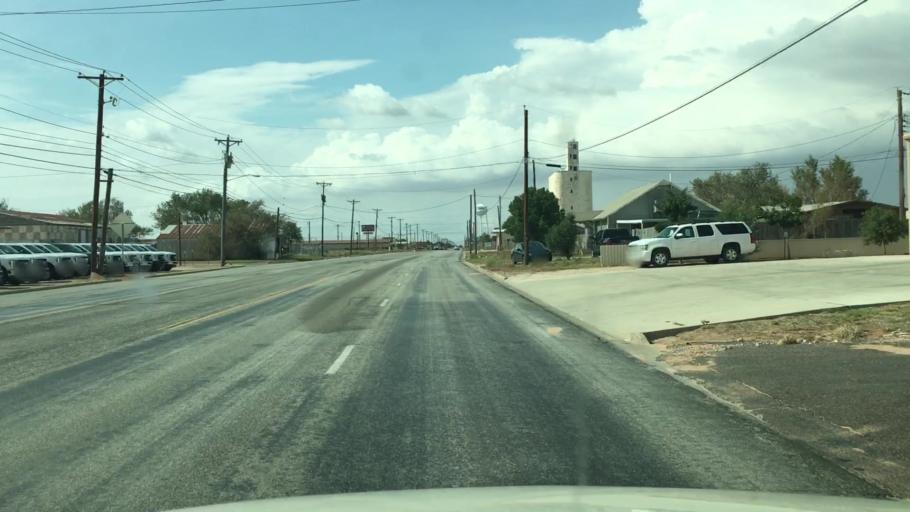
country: US
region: Texas
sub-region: Dawson County
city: Lamesa
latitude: 32.7231
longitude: -101.9461
